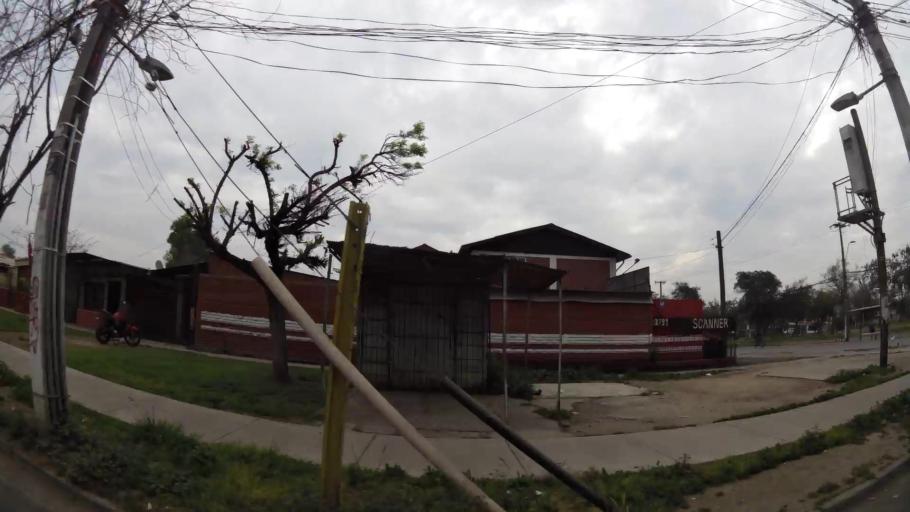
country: CL
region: Santiago Metropolitan
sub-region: Provincia de Santiago
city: Villa Presidente Frei, Nunoa, Santiago, Chile
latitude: -33.4742
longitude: -70.5922
